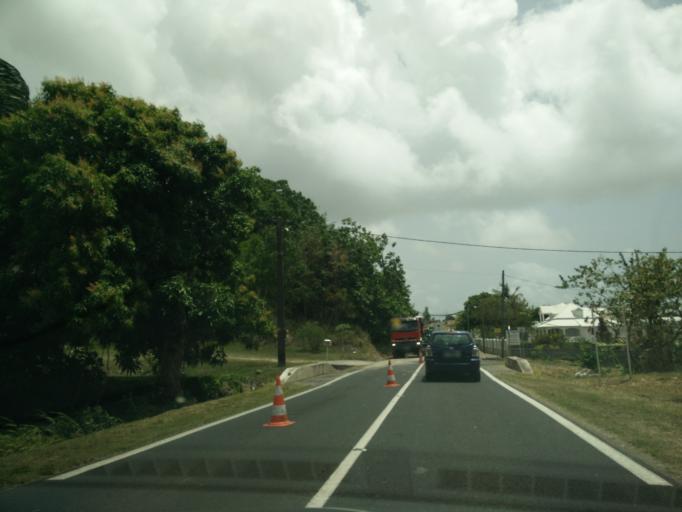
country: GP
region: Guadeloupe
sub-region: Guadeloupe
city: Petit-Canal
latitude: 16.3561
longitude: -61.4559
